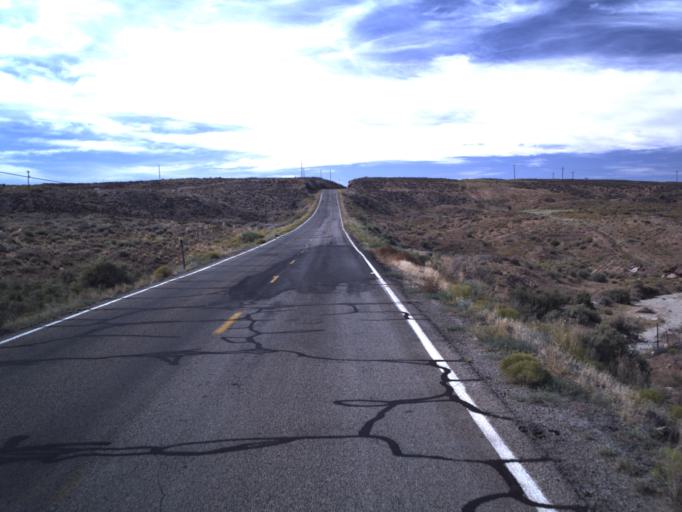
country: US
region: Utah
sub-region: San Juan County
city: Blanding
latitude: 37.2922
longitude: -109.2880
